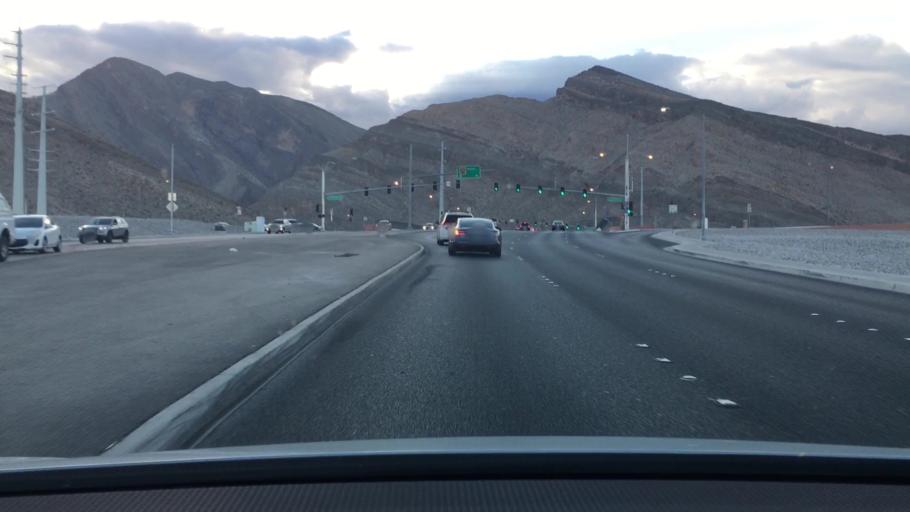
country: US
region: Nevada
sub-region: Clark County
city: Summerlin South
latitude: 36.2185
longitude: -115.3256
